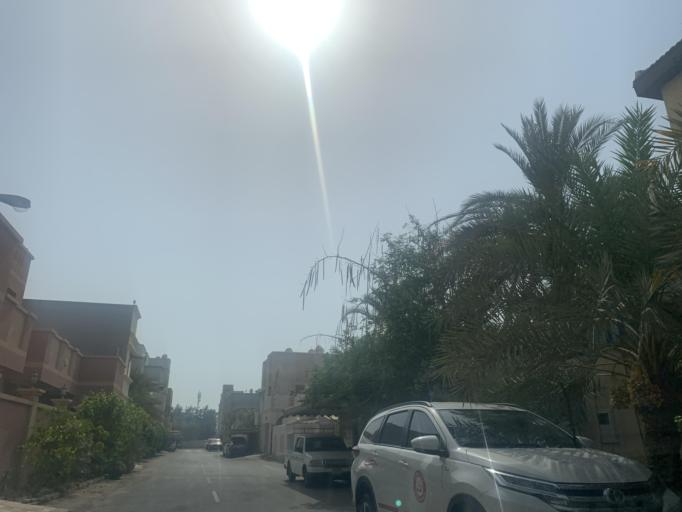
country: BH
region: Manama
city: Jidd Hafs
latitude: 26.2105
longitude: 50.4673
